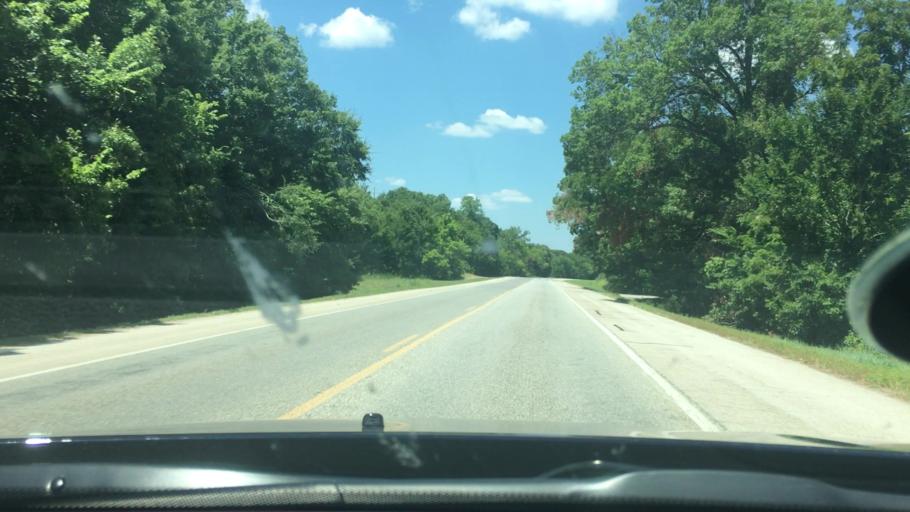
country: US
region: Oklahoma
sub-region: Marshall County
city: Oakland
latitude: 34.1735
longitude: -96.8491
